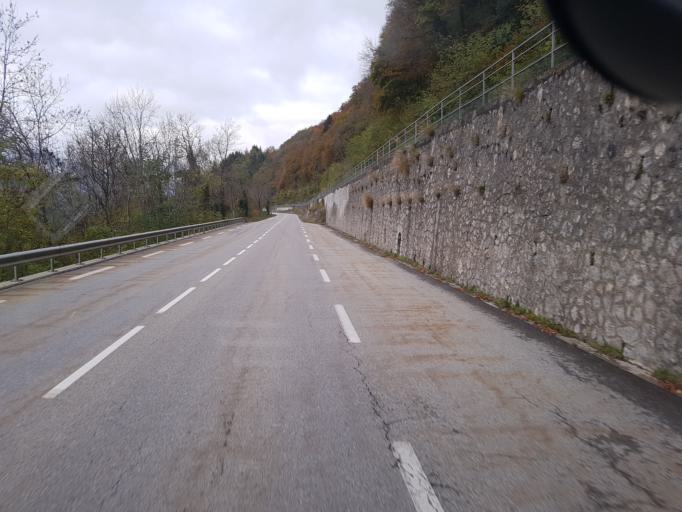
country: FR
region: Rhone-Alpes
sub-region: Departement de l'Isere
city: La Motte-Saint-Martin
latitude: 44.9387
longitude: 5.6404
